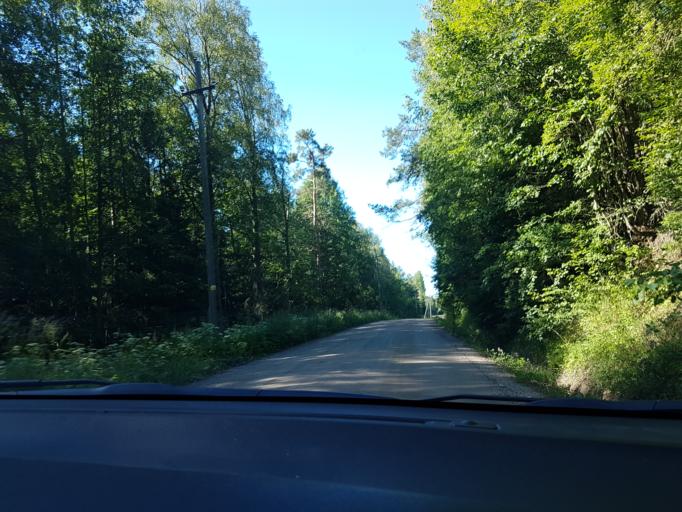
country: FI
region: Uusimaa
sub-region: Helsinki
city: Sibbo
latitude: 60.2827
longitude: 25.2388
